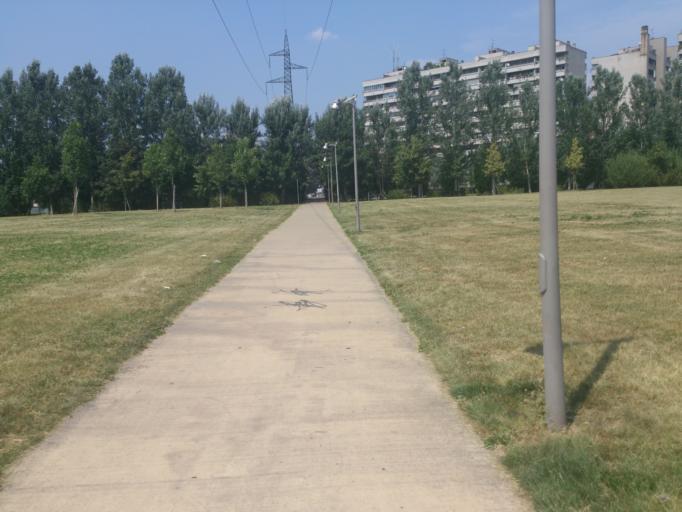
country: IT
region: Lombardy
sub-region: Citta metropolitana di Milano
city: Cologno Monzese
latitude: 45.5175
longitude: 9.2745
